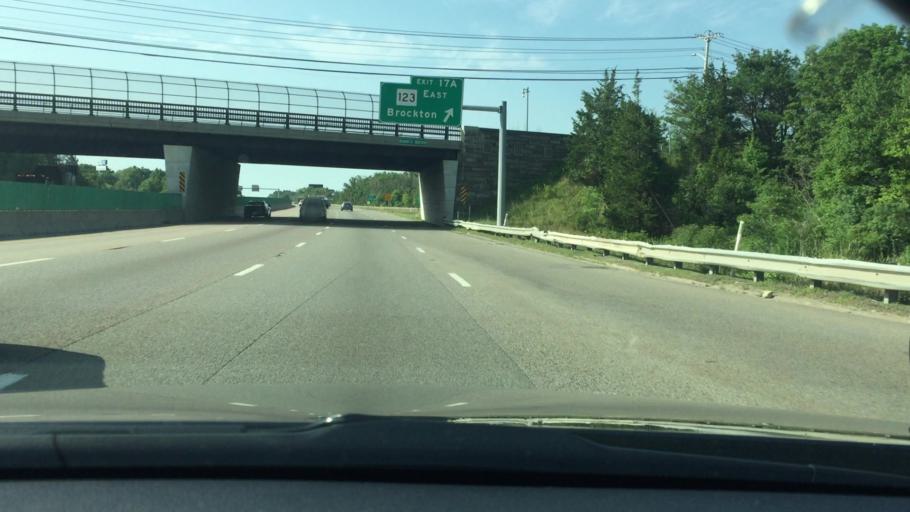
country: US
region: Massachusetts
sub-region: Plymouth County
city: Brockton
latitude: 42.0627
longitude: -71.0619
